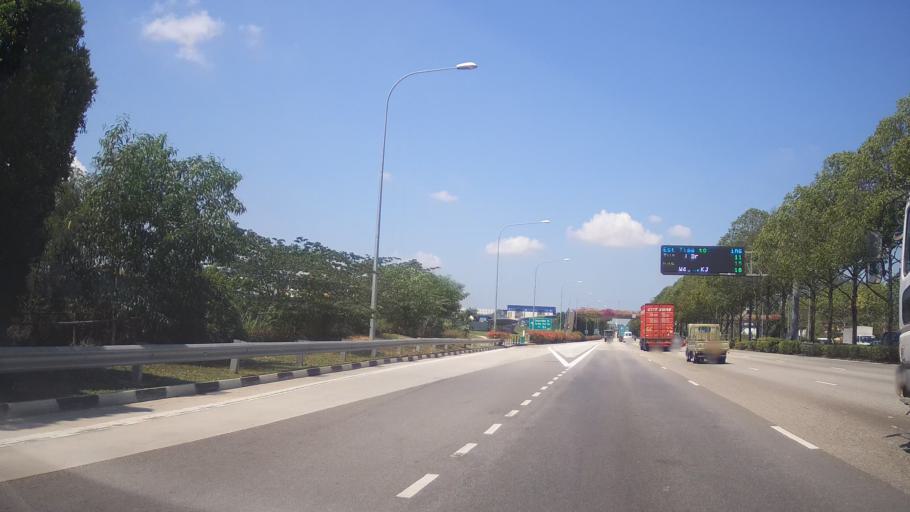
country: SG
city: Singapore
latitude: 1.3257
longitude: 103.7295
